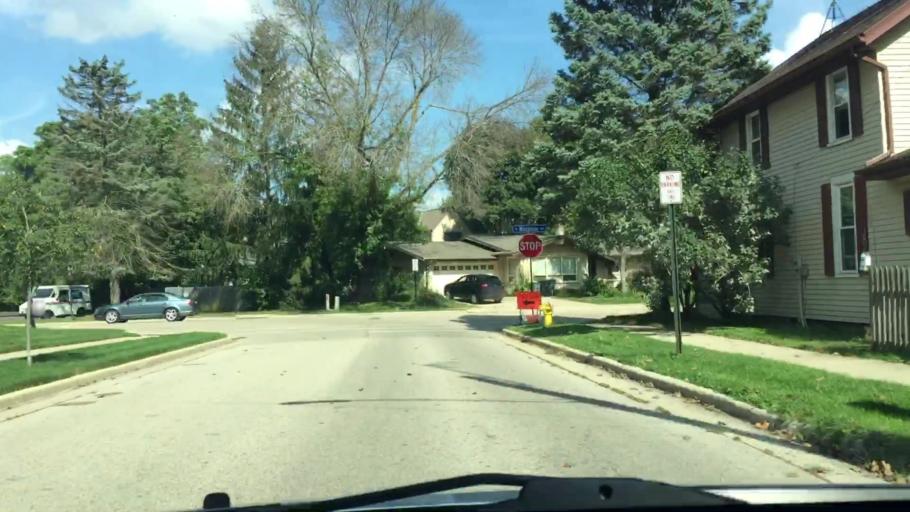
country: US
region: Wisconsin
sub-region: Waukesha County
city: Oconomowoc
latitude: 43.1144
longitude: -88.5121
